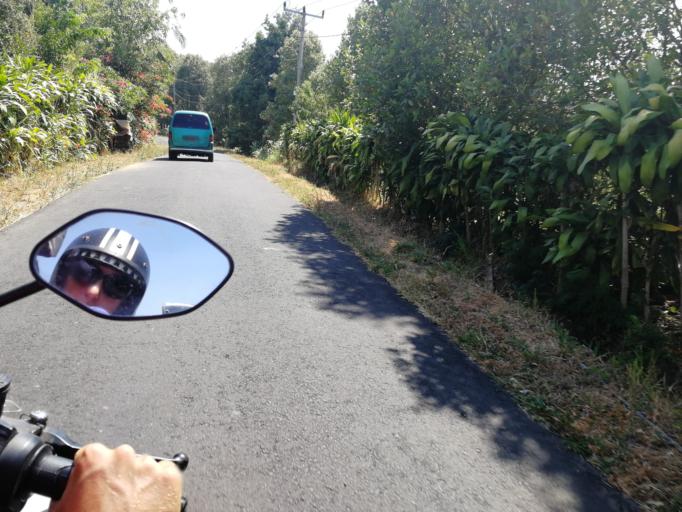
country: ID
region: Bali
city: Banjar Kedisan
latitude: -8.1613
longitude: 115.3054
